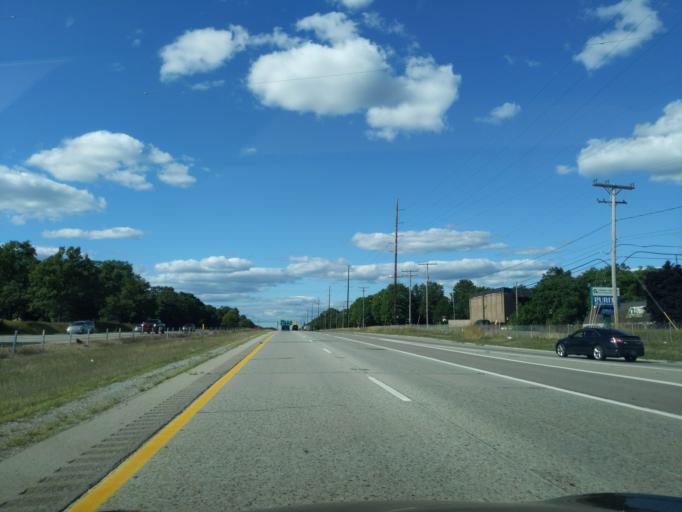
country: US
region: Michigan
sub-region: Muskegon County
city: Muskegon
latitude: 43.2362
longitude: -86.2046
